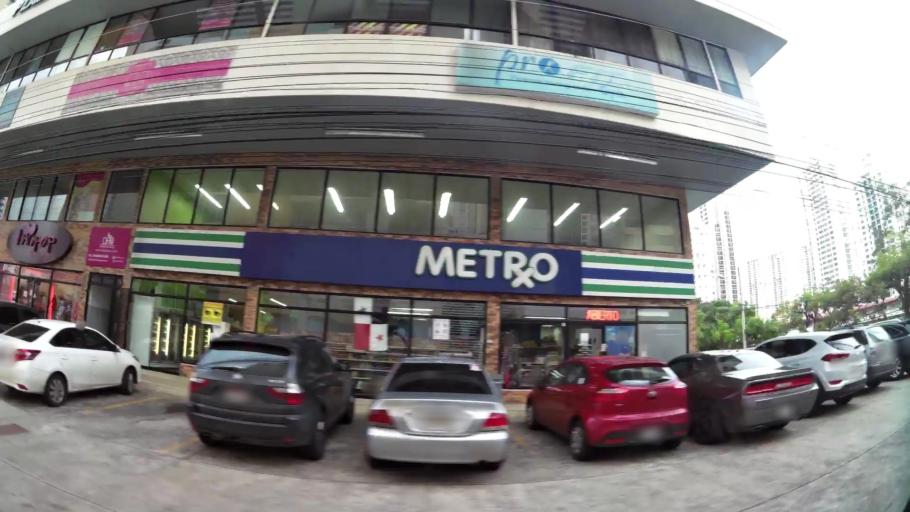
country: PA
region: Panama
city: Panama
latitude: 8.9899
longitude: -79.5049
